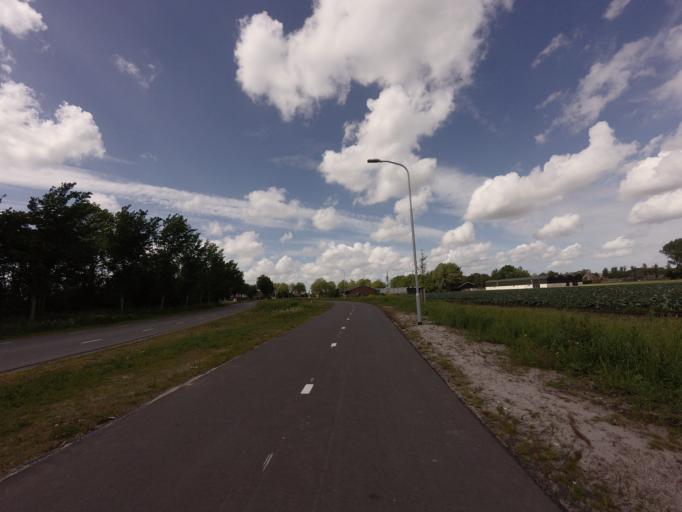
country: NL
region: North Holland
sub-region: Gemeente Hoorn
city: Hoorn
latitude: 52.6841
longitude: 5.0870
